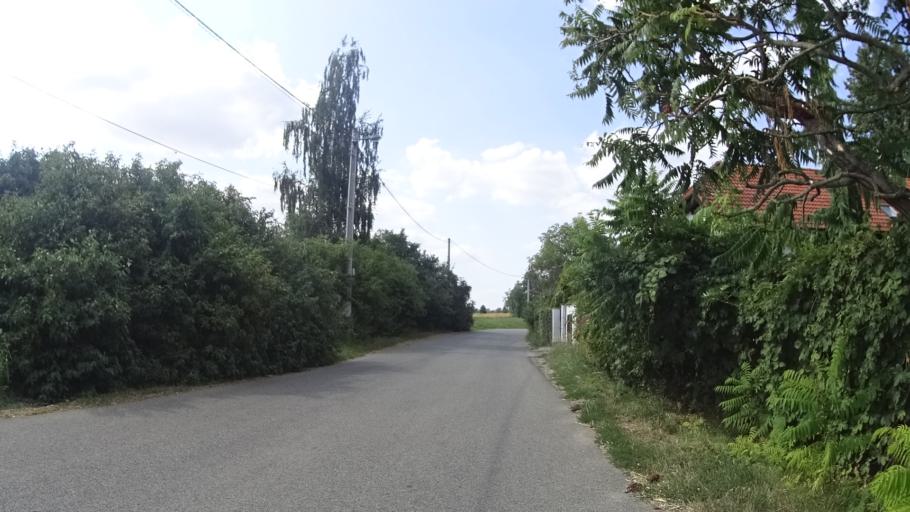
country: CZ
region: Kralovehradecky
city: Liban
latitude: 50.4058
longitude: 15.2715
